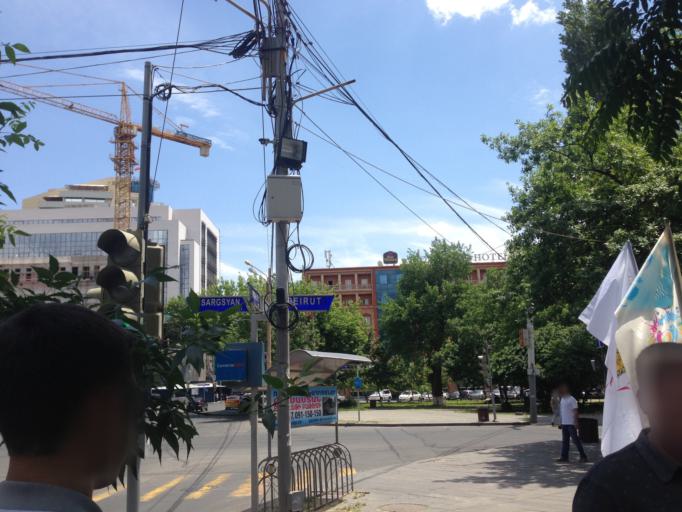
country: AM
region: Yerevan
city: Yerevan
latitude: 40.1764
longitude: 44.5084
